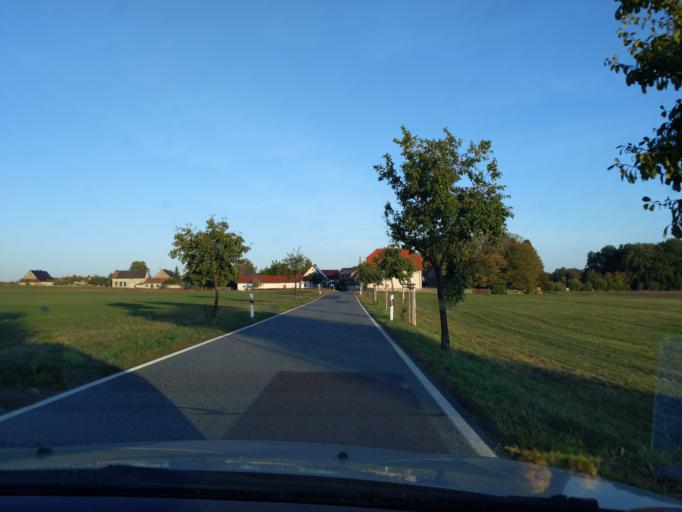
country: DE
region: Saxony
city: Guttau
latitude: 51.2745
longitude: 14.5766
